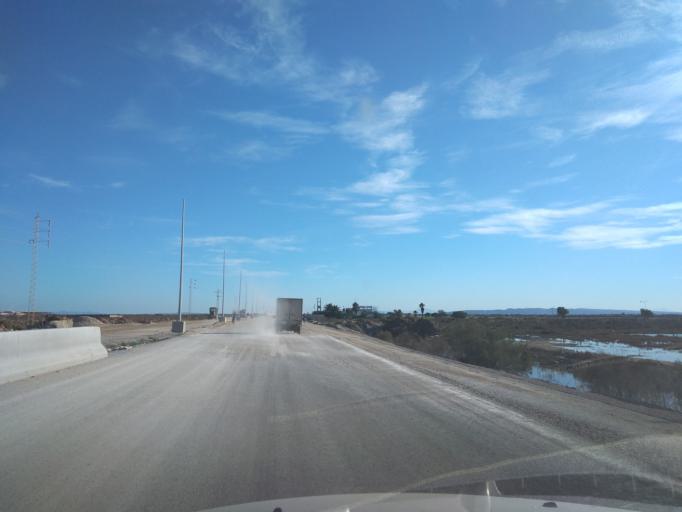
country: TN
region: Ariana
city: Qal'at al Andalus
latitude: 37.0444
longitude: 10.1274
